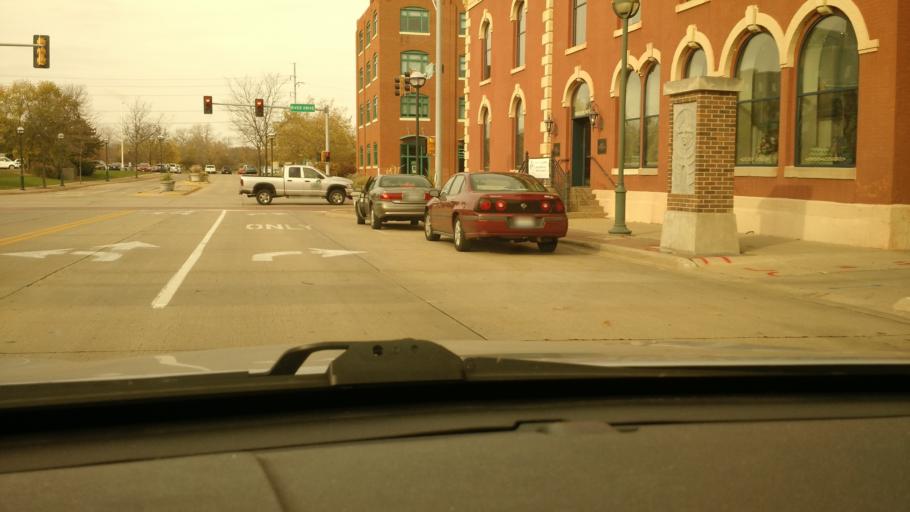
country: US
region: Illinois
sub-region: Rock Island County
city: Moline
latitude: 41.5078
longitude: -90.5173
